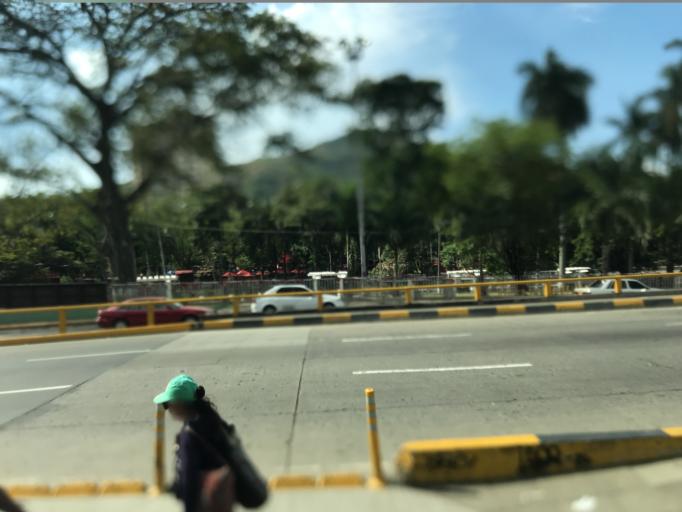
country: CO
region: Valle del Cauca
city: Cali
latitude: 3.4551
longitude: -76.5314
